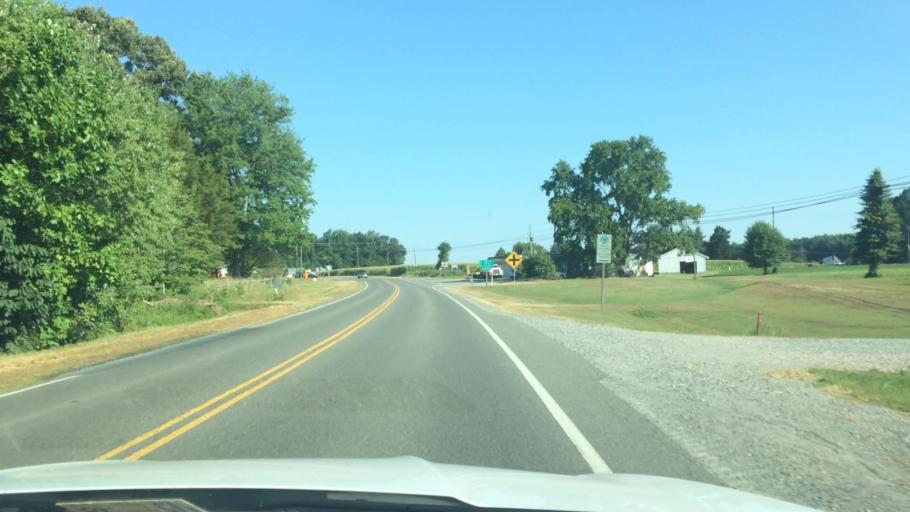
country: US
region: Virginia
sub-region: Lancaster County
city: Lancaster
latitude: 37.7946
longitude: -76.5204
